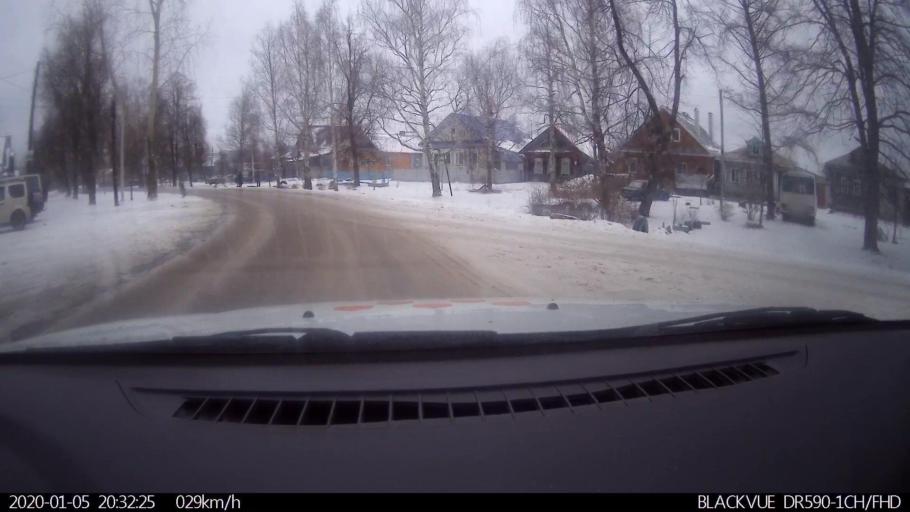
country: RU
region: Nizjnij Novgorod
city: Lukino
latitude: 56.4120
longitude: 43.7287
